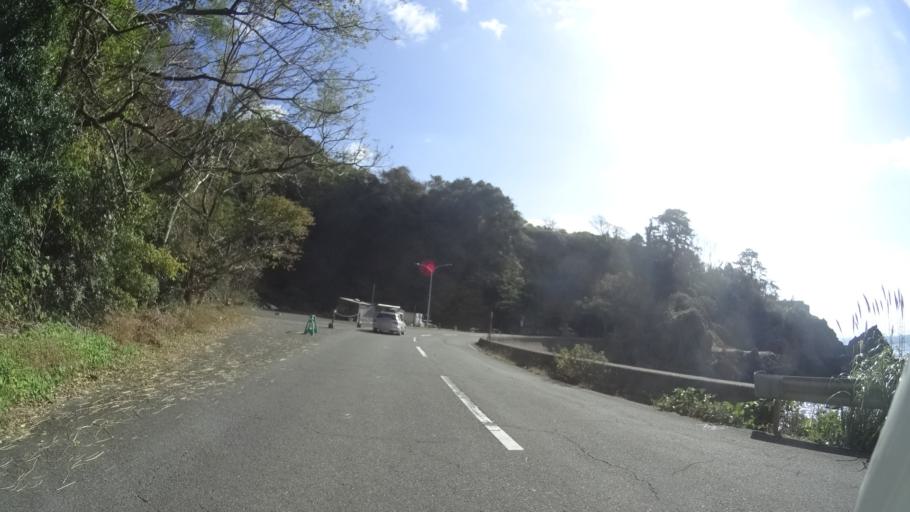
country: JP
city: Asahi
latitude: 35.9607
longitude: 135.9733
